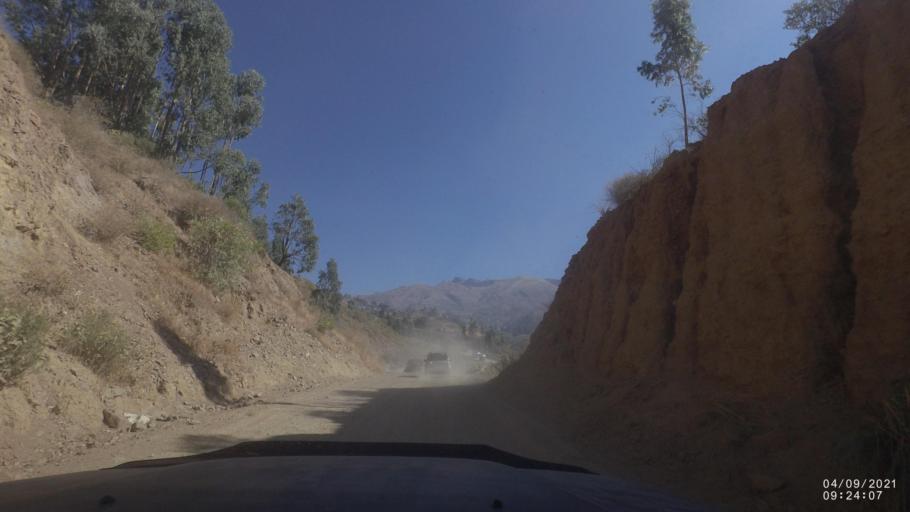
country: BO
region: Cochabamba
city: Sipe Sipe
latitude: -17.3607
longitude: -66.3675
